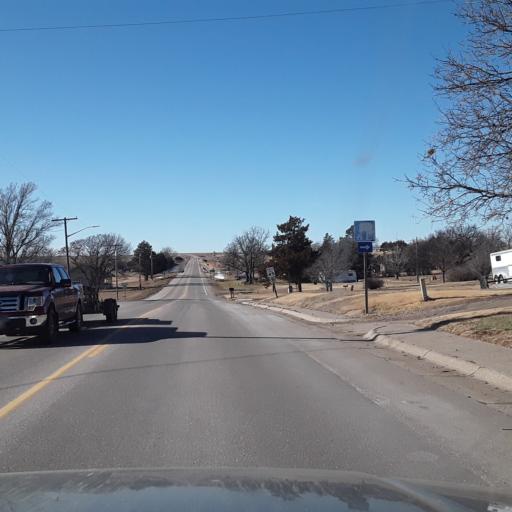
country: US
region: Nebraska
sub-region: Dawson County
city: Gothenburg
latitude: 40.7058
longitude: -100.2164
